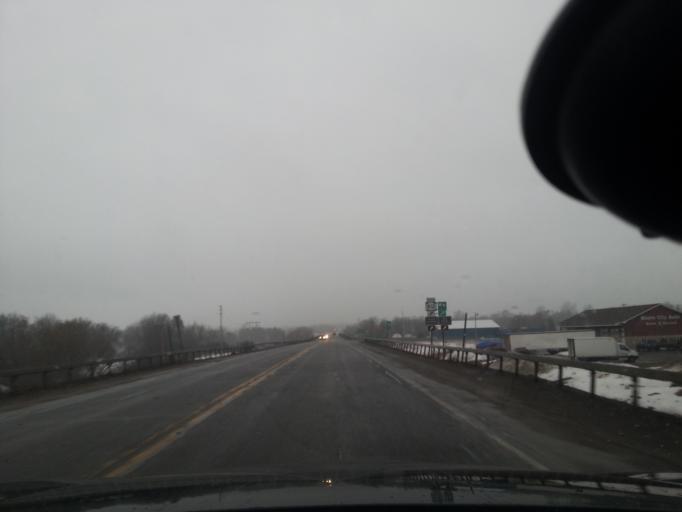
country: US
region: New York
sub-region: St. Lawrence County
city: Ogdensburg
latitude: 44.6858
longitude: -75.4840
